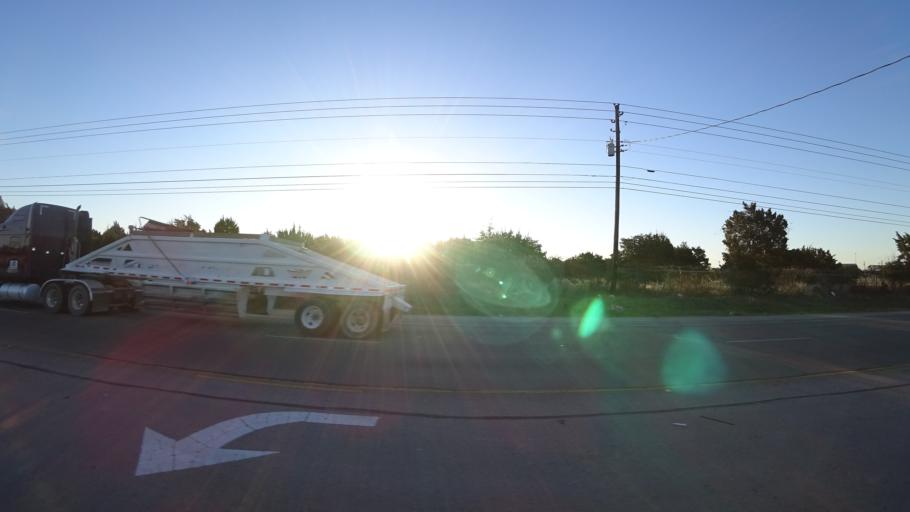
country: US
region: Texas
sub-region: Travis County
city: Hornsby Bend
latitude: 30.3001
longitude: -97.6223
